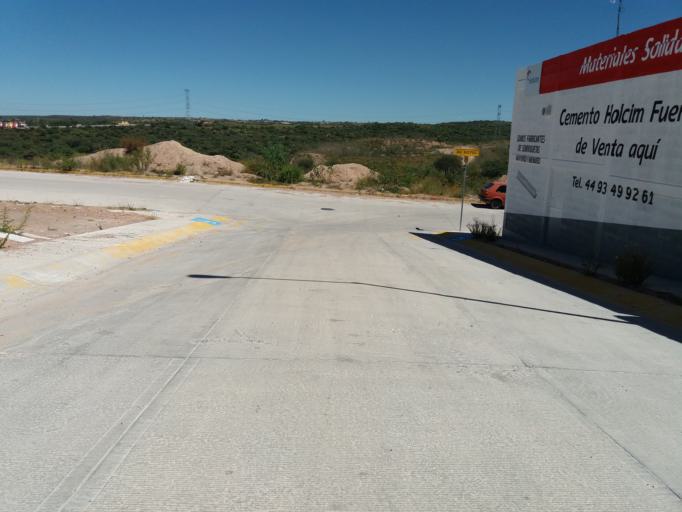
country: MX
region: Aguascalientes
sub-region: Aguascalientes
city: Cumbres III
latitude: 21.8732
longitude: -102.2278
